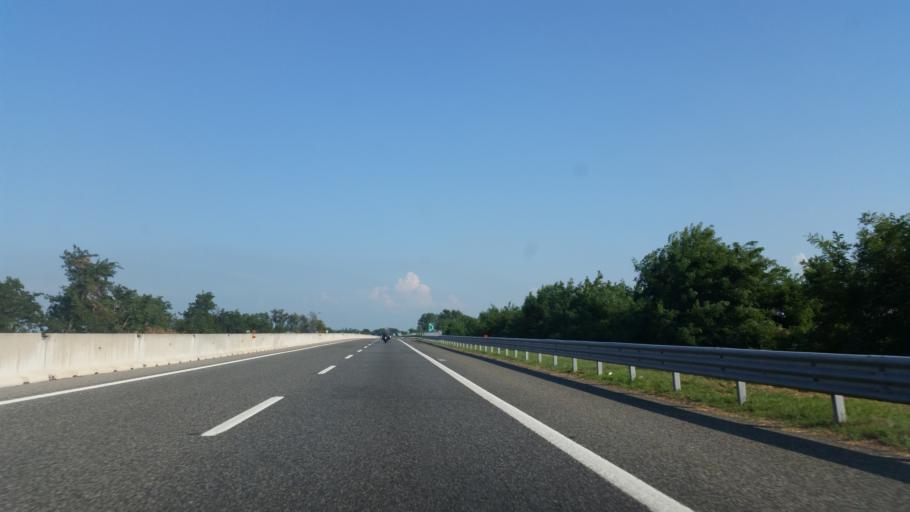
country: IT
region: Piedmont
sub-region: Provincia di Vercelli
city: Asigliano Vercellese
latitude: 45.2657
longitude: 8.4254
